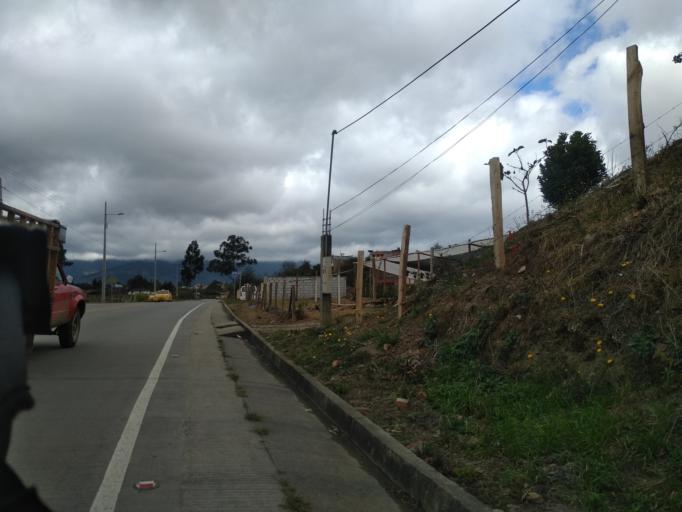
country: EC
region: Loja
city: Loja
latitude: -3.9539
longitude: -79.2471
